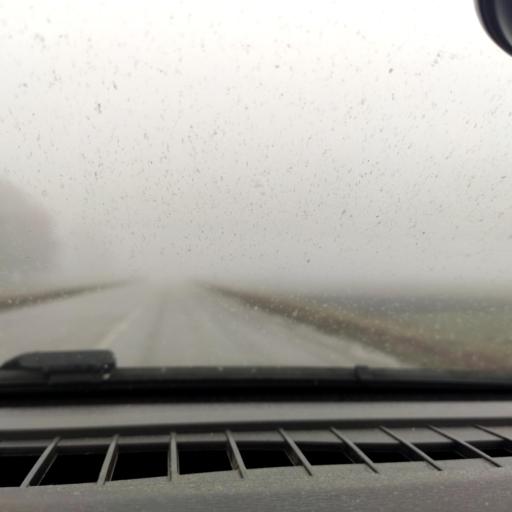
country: RU
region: Belgorod
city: Ilovka
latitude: 50.7435
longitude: 38.7102
